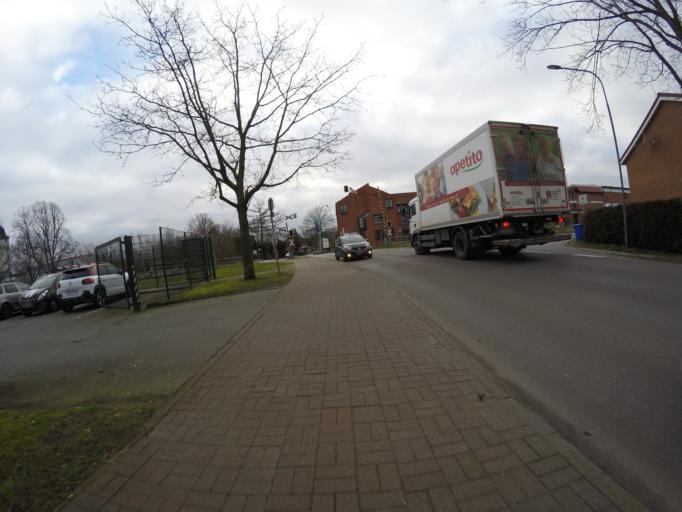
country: DE
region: Schleswig-Holstein
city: Alveslohe
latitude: 53.7919
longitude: 9.9159
